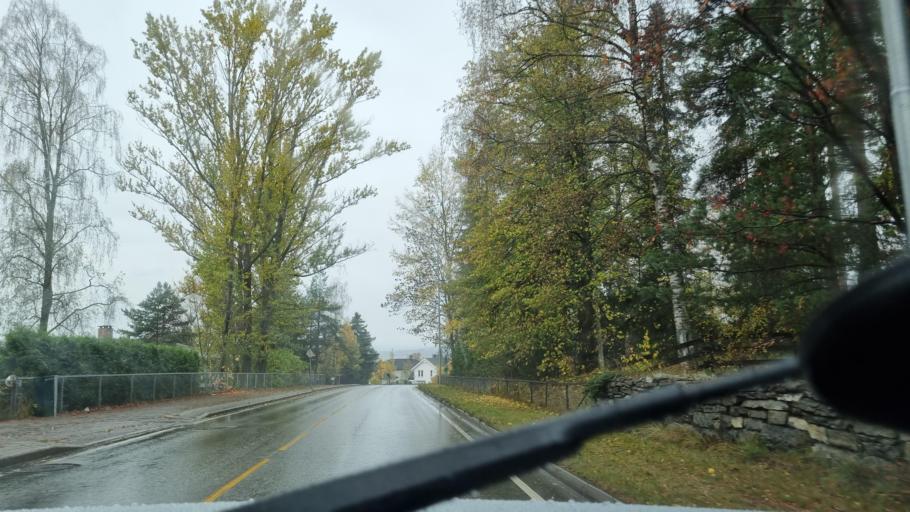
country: NO
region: Hedmark
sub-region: Hamar
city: Hamar
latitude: 60.8091
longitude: 11.0547
